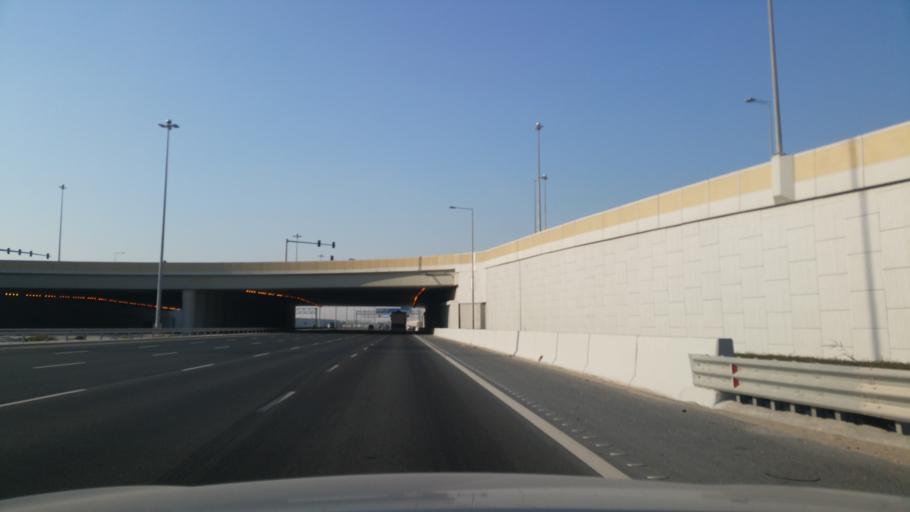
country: QA
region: Al Wakrah
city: Al Wakrah
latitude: 25.1482
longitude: 51.5772
